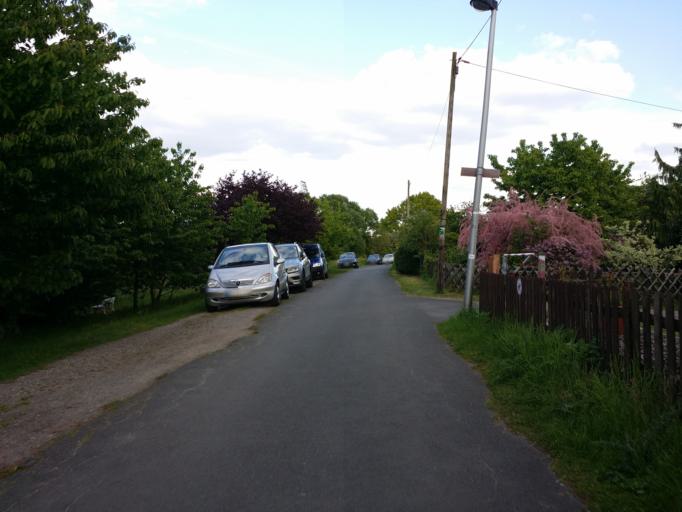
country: DE
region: Bremen
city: Bremen
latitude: 53.0671
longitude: 8.8301
